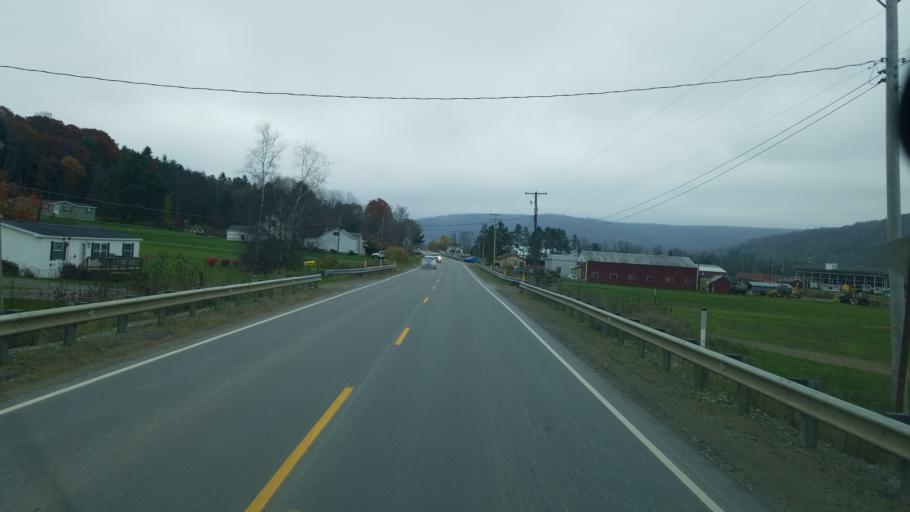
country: US
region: Pennsylvania
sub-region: McKean County
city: Smethport
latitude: 41.8074
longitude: -78.4200
